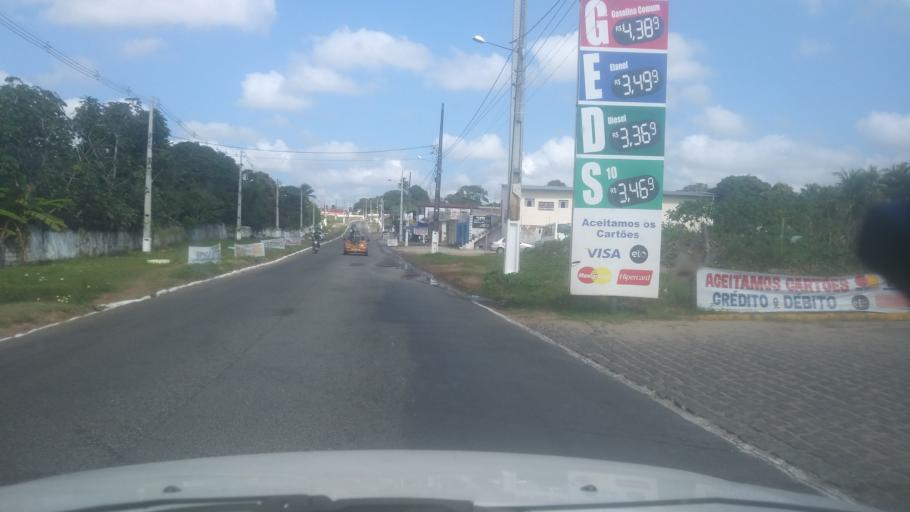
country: BR
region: Rio Grande do Norte
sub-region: Extremoz
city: Extremoz
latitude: -5.7040
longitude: -35.2826
